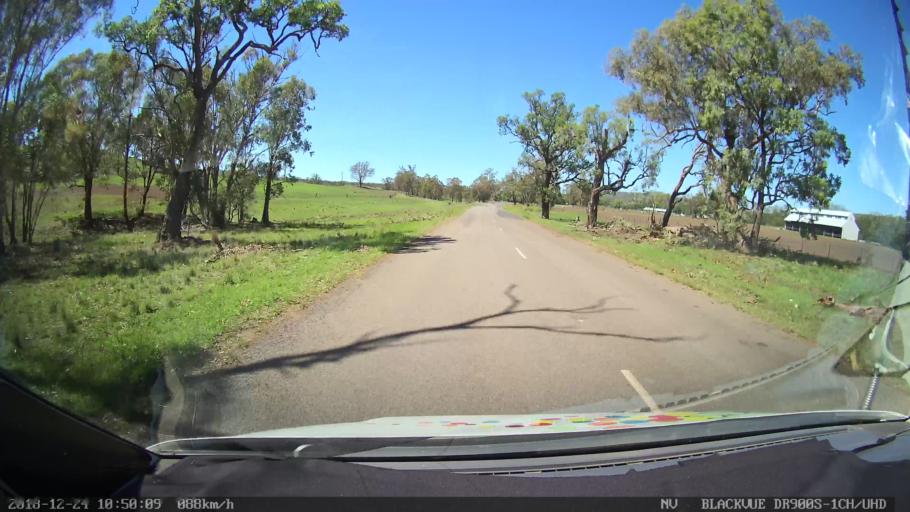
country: AU
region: New South Wales
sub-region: Upper Hunter Shire
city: Merriwa
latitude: -31.9566
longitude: 150.4246
